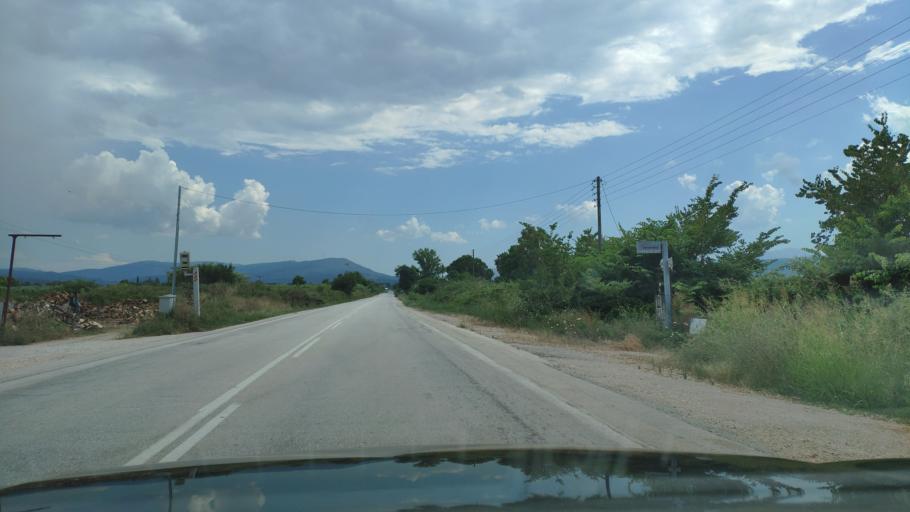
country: GR
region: West Greece
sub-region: Nomos Aitolias kai Akarnanias
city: Krikellos
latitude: 38.9423
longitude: 21.1767
